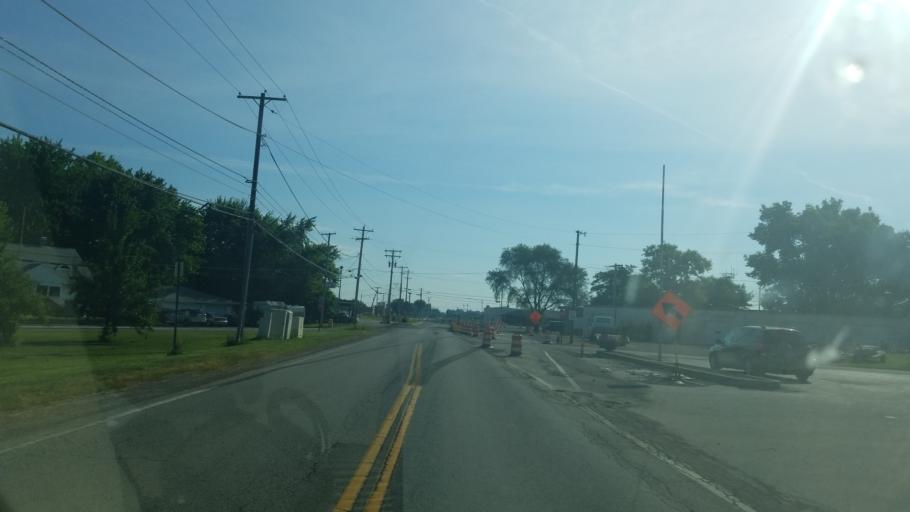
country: US
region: Ohio
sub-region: Hancock County
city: Findlay
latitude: 41.0206
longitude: -83.6713
